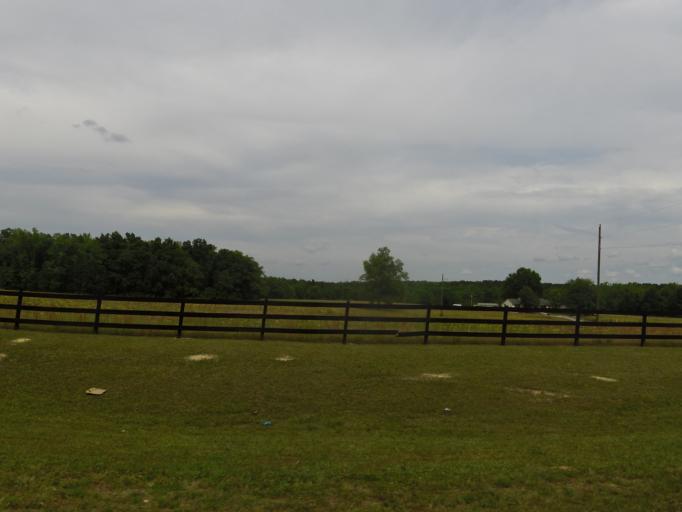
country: US
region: Georgia
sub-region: McDuffie County
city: Thomson
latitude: 33.3798
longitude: -82.4708
